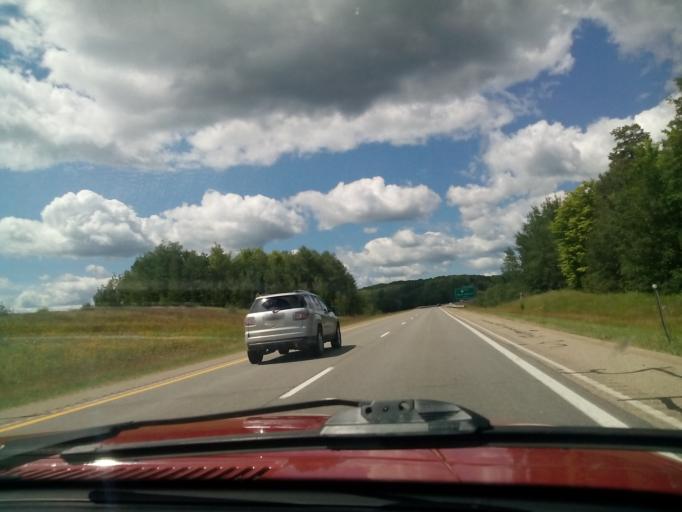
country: US
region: Michigan
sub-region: Ogemaw County
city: West Branch
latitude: 44.2604
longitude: -84.2569
